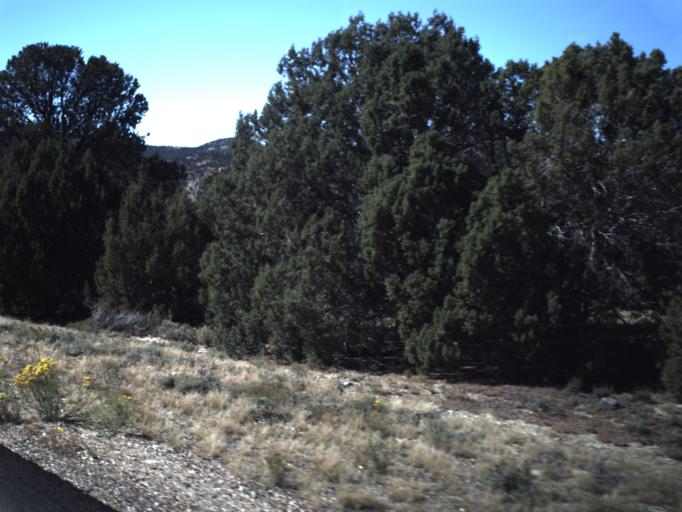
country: US
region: Utah
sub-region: Garfield County
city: Panguitch
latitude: 37.6183
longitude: -111.8781
